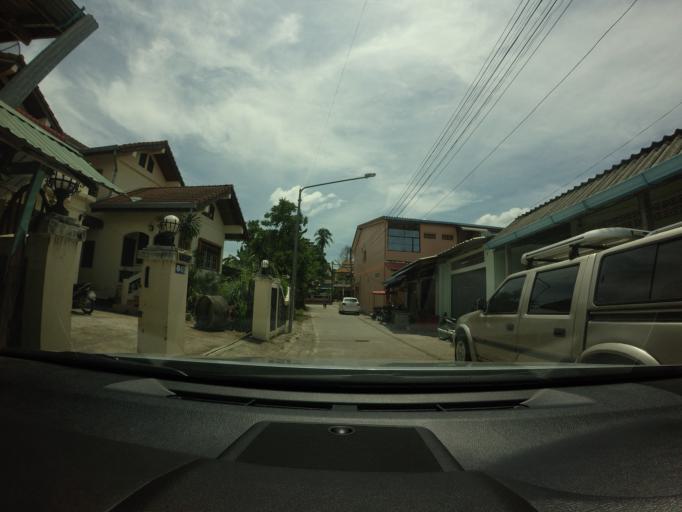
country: TH
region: Narathiwat
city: Rueso
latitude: 6.3954
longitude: 101.5169
